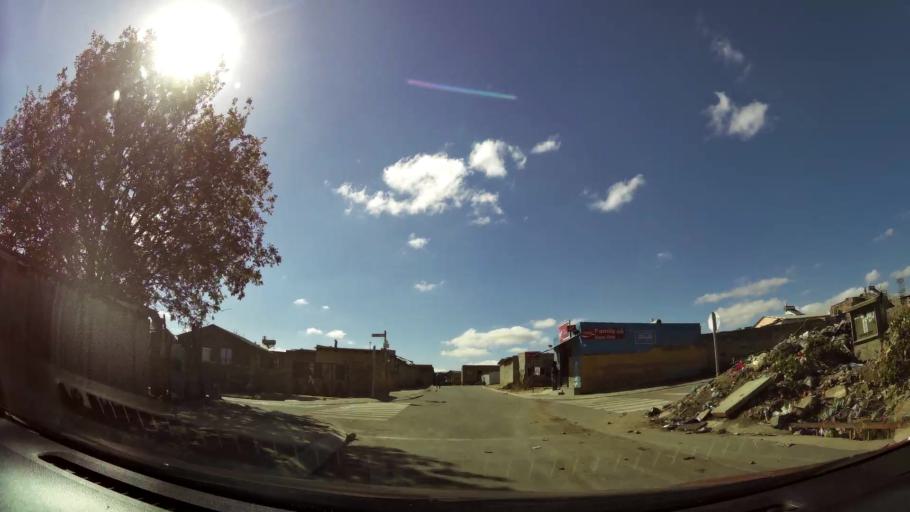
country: ZA
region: Gauteng
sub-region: City of Johannesburg Metropolitan Municipality
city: Midrand
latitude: -26.0340
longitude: 28.1611
